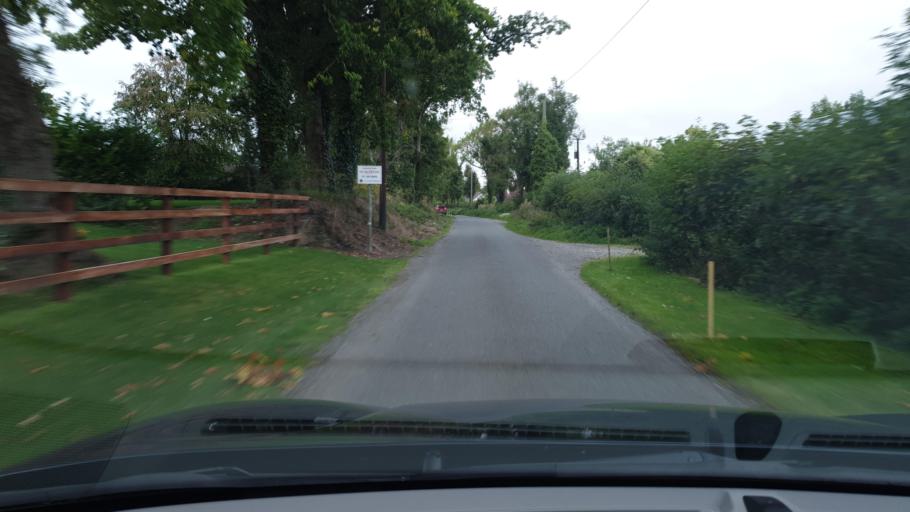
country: IE
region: Leinster
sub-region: An Mhi
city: Ratoath
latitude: 53.5253
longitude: -6.4989
